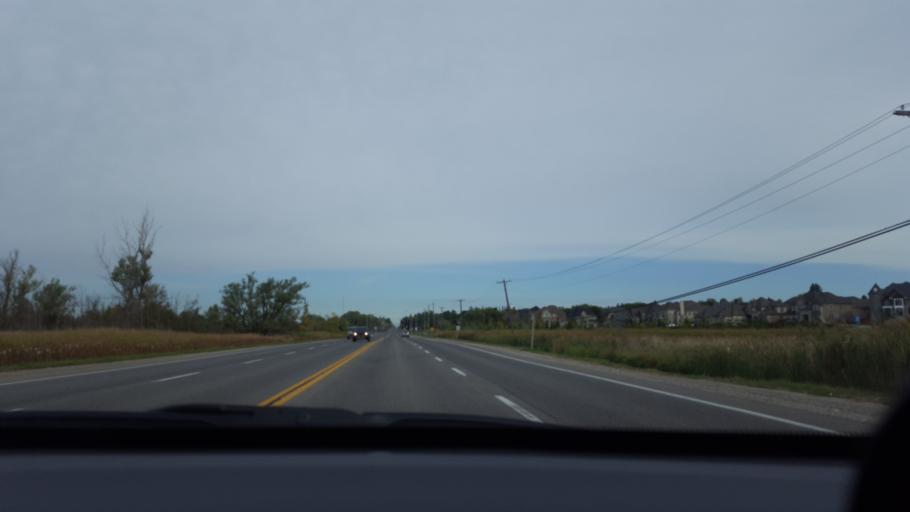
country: CA
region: Ontario
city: Vaughan
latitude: 43.9159
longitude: -79.5247
